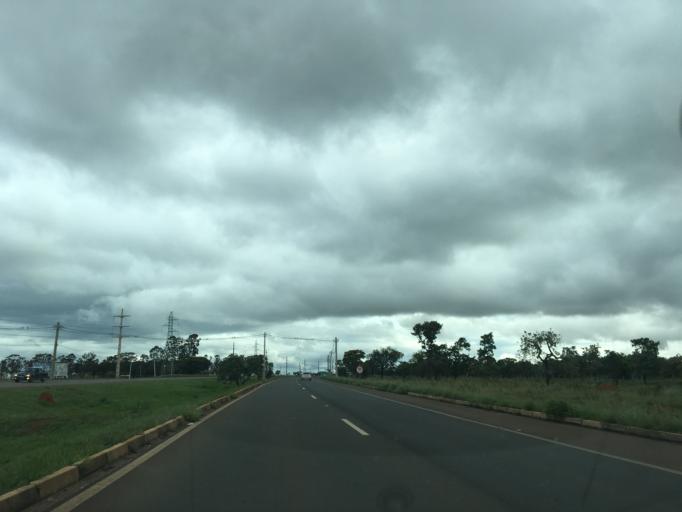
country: BR
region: Federal District
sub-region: Brasilia
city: Brasilia
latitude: -15.8953
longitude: -47.8198
